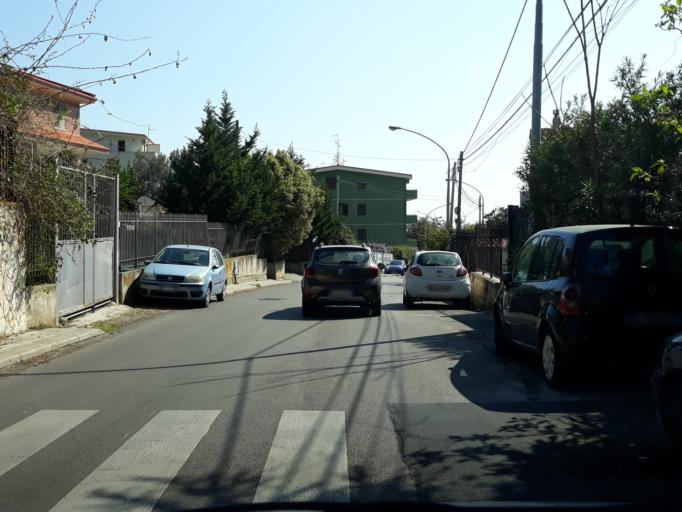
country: IT
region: Sicily
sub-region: Palermo
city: Piano dei Geli
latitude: 38.1174
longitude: 13.2913
